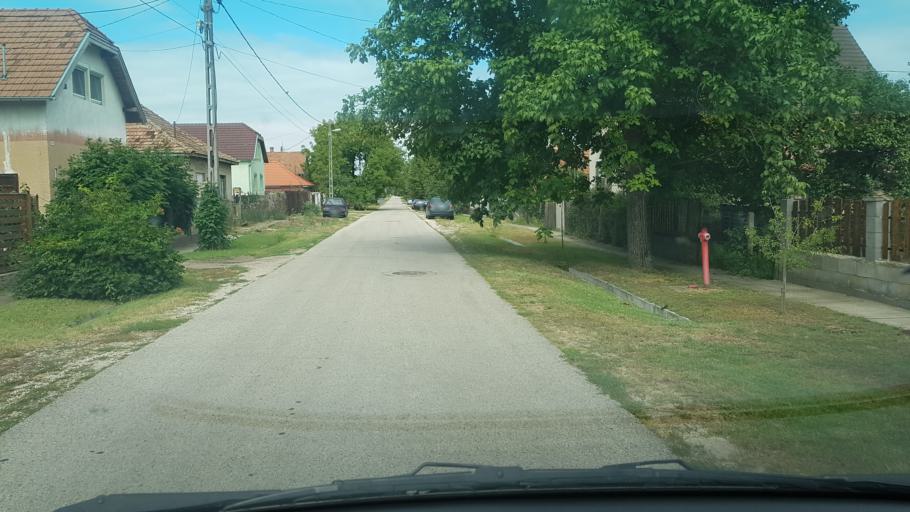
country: HU
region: Pest
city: Dunavarsany
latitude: 47.2792
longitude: 19.0604
